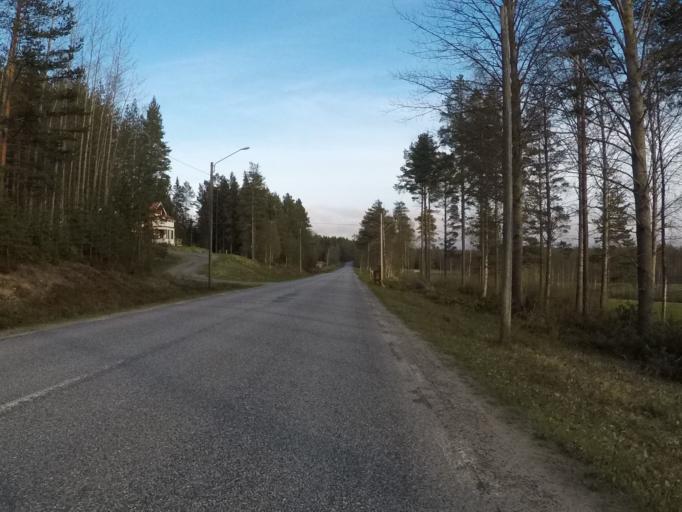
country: SE
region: Vaesterbotten
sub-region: Robertsfors Kommun
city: Robertsfors
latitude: 63.9958
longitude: 20.8073
